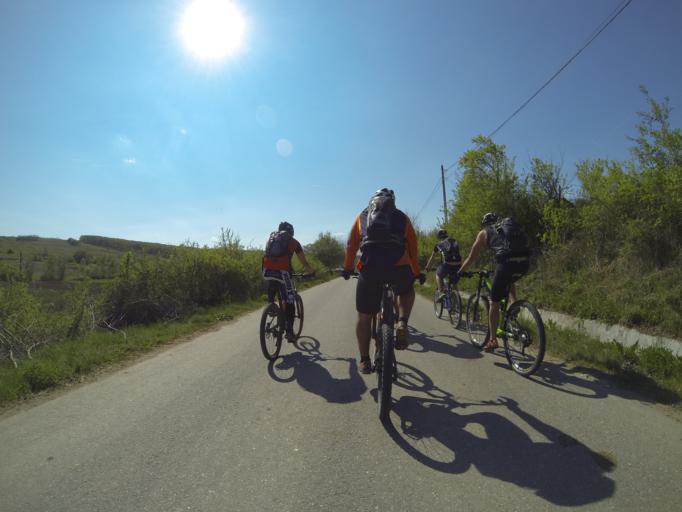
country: RO
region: Gorj
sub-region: Comuna Crusetu
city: Crusetu
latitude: 44.6181
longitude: 23.6649
